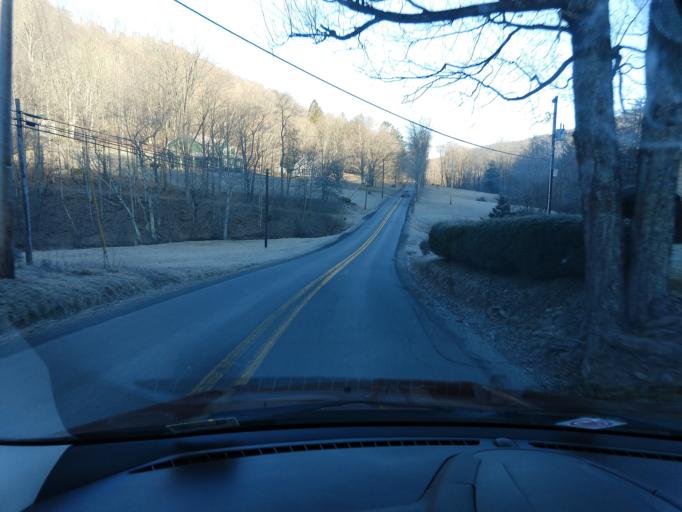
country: US
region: West Virginia
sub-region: Greenbrier County
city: Rainelle
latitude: 37.9473
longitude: -80.7346
